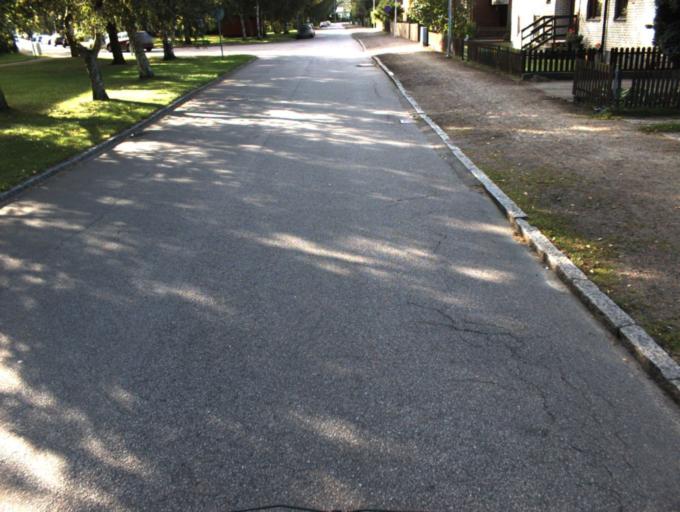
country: SE
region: Skane
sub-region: Helsingborg
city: Helsingborg
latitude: 56.0214
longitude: 12.7244
